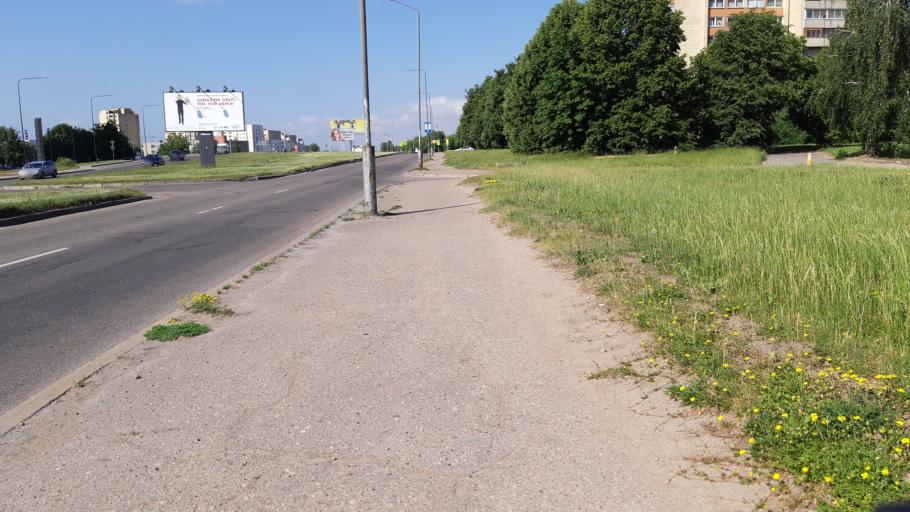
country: LT
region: Kauno apskritis
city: Dainava (Kaunas)
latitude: 54.9184
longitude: 23.9885
